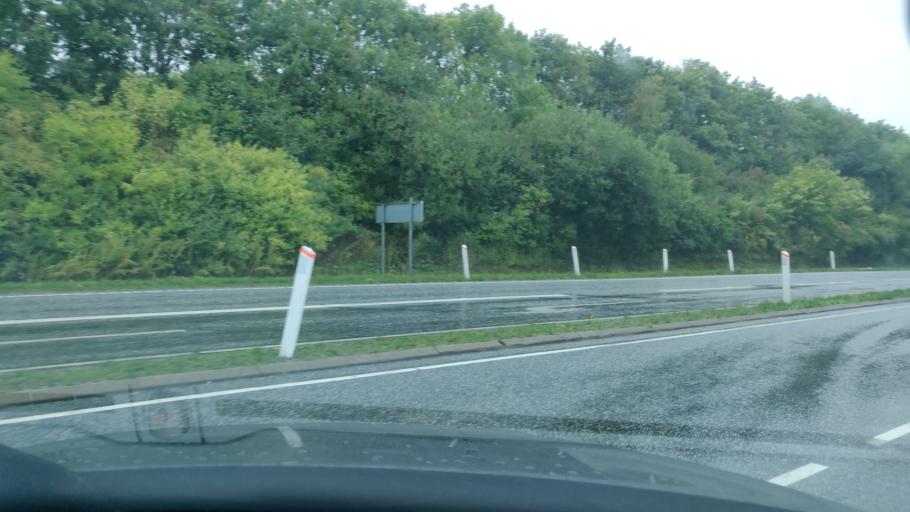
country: DK
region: North Denmark
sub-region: Thisted Kommune
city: Thisted
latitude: 56.8840
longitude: 8.5936
